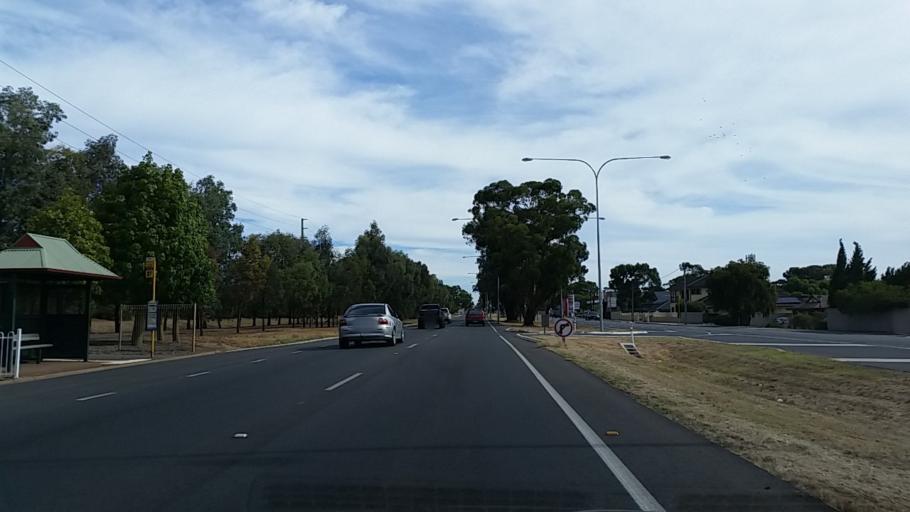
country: AU
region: South Australia
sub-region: Playford
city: Smithfield
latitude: -34.6800
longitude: 138.6957
